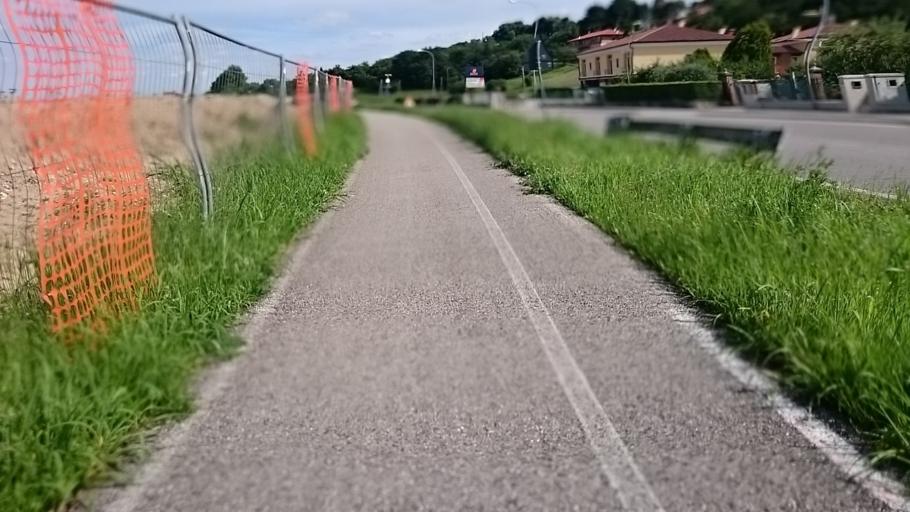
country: IT
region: Veneto
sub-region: Provincia di Vicenza
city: Longare
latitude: 45.4941
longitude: 11.5907
